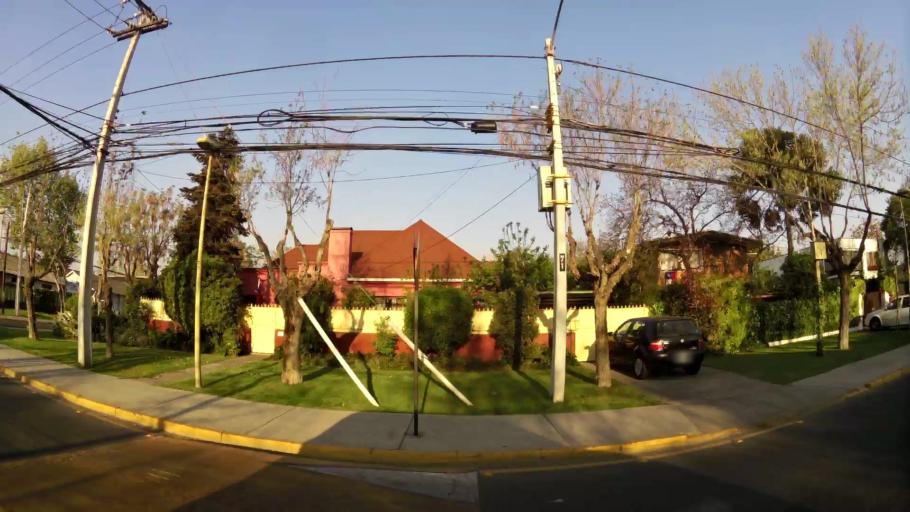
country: CL
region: Santiago Metropolitan
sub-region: Provincia de Santiago
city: Villa Presidente Frei, Nunoa, Santiago, Chile
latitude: -33.3974
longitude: -70.5545
